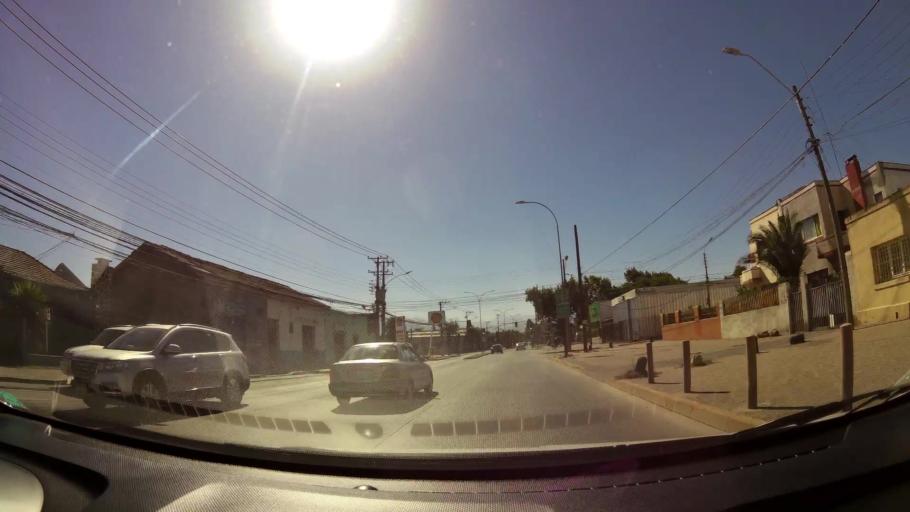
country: CL
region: O'Higgins
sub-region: Provincia de Cachapoal
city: Rancagua
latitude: -34.1739
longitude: -70.7482
